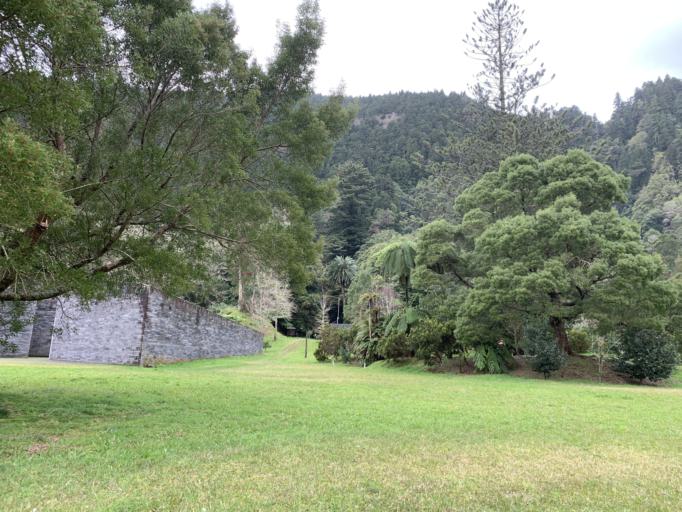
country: PT
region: Azores
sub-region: Povoacao
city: Furnas
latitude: 37.7519
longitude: -25.3375
